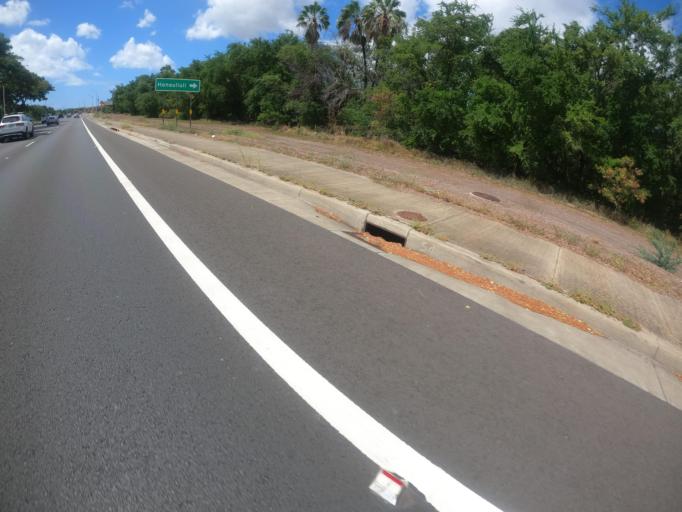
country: US
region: Hawaii
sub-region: Honolulu County
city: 'Ewa Gentry
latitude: 21.3626
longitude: -158.0281
